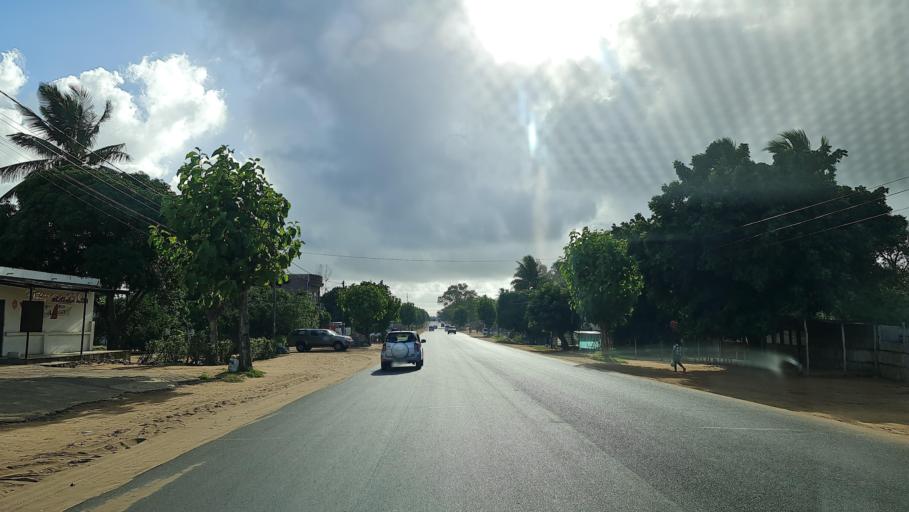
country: MZ
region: Gaza
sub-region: Xai-Xai District
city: Xai-Xai
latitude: -25.0566
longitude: 33.6845
